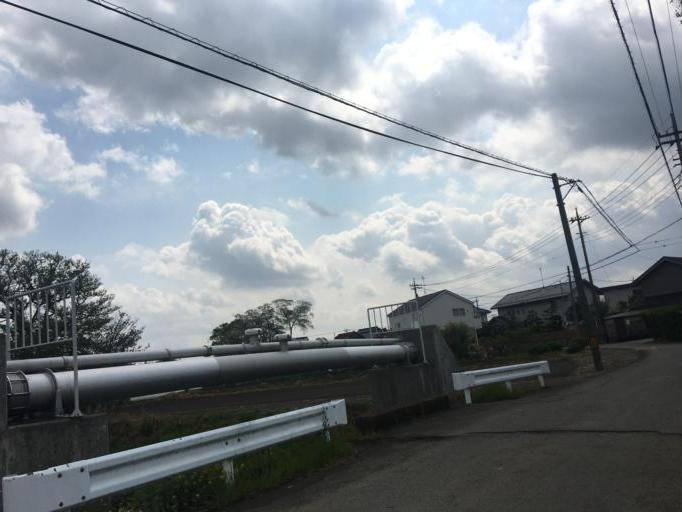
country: JP
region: Saitama
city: Kawagoe
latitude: 35.8958
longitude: 139.5057
